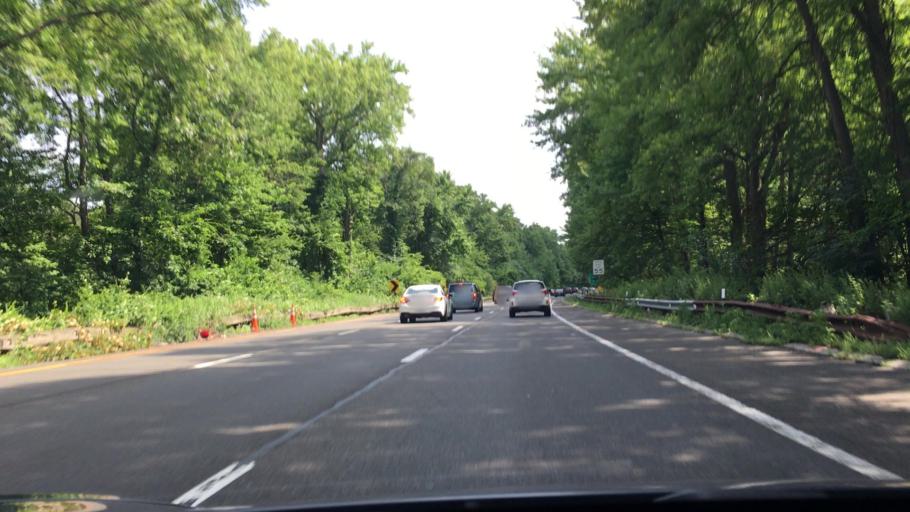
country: US
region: New York
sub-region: Nassau County
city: Freeport
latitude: 40.6700
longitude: -73.5697
